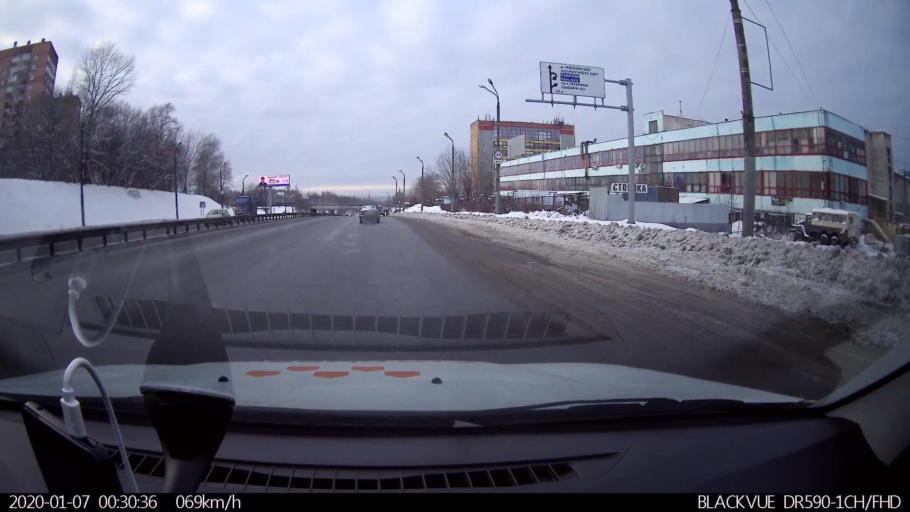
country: RU
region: Nizjnij Novgorod
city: Nizhniy Novgorod
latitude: 56.2437
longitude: 43.9700
